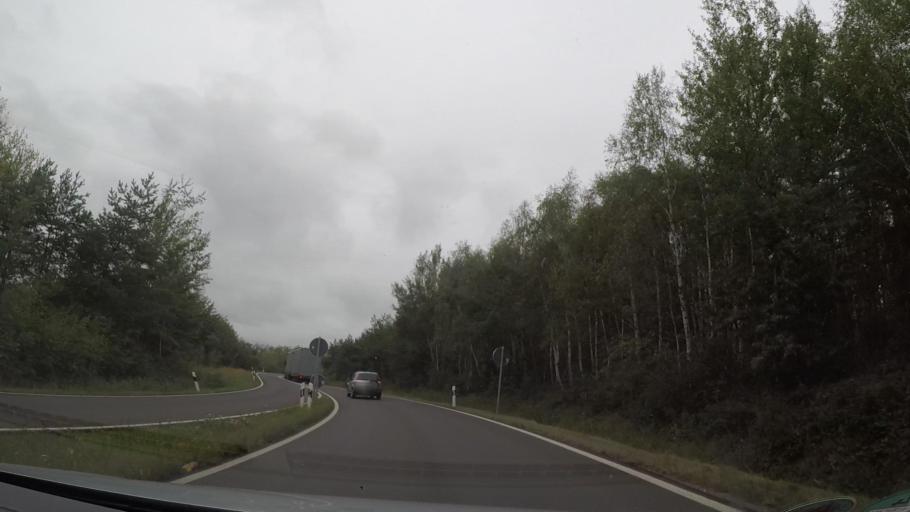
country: DE
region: Saxony-Anhalt
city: Beendorf
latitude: 52.2177
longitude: 11.0771
